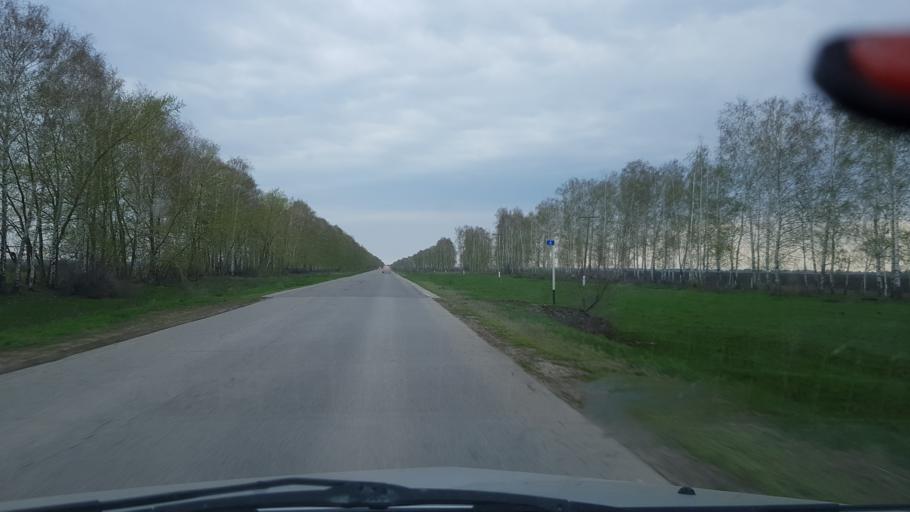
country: RU
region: Samara
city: Tol'yatti
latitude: 53.6594
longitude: 49.2310
